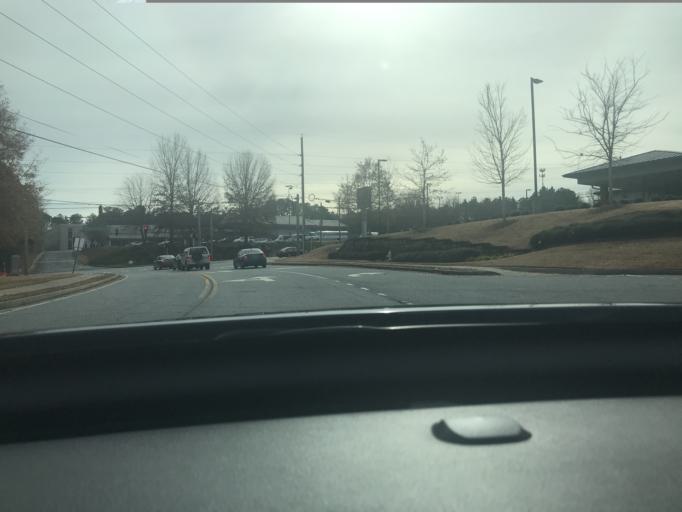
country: US
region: Georgia
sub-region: Gwinnett County
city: Mountain Park
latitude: 33.8707
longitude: -84.0904
